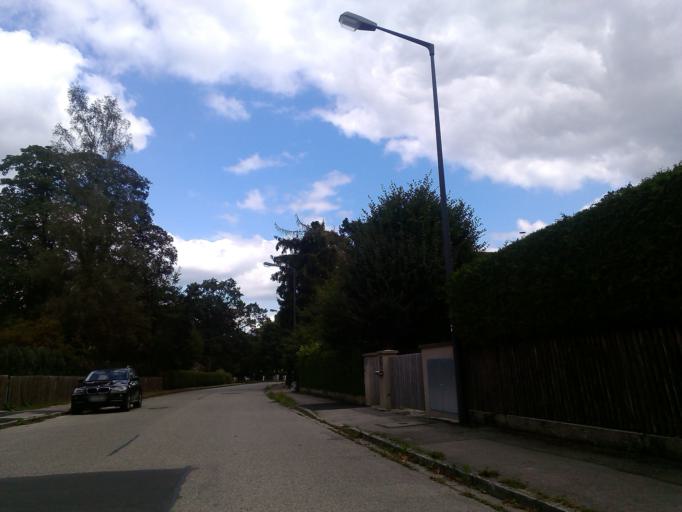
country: DE
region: Bavaria
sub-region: Upper Bavaria
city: Grafelfing
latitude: 48.1160
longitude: 11.4222
